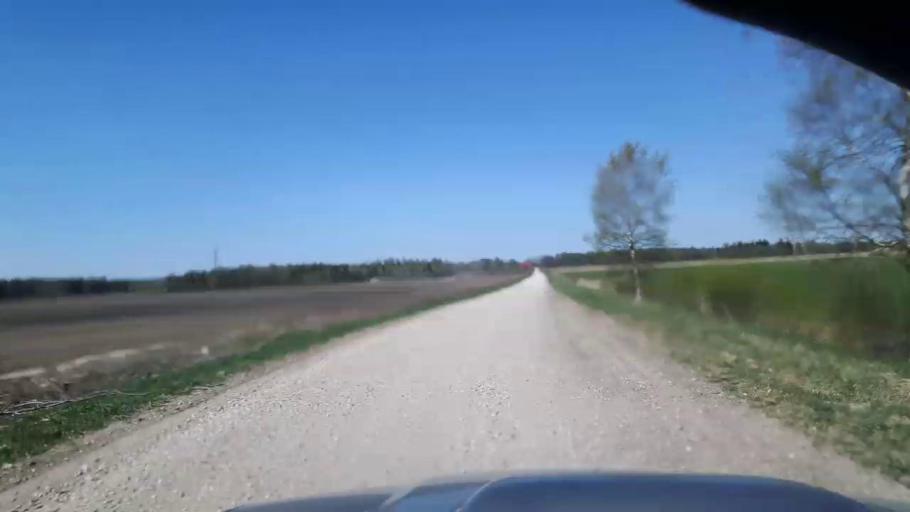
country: EE
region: Paernumaa
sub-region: Sindi linn
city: Sindi
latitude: 58.4763
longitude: 24.7463
